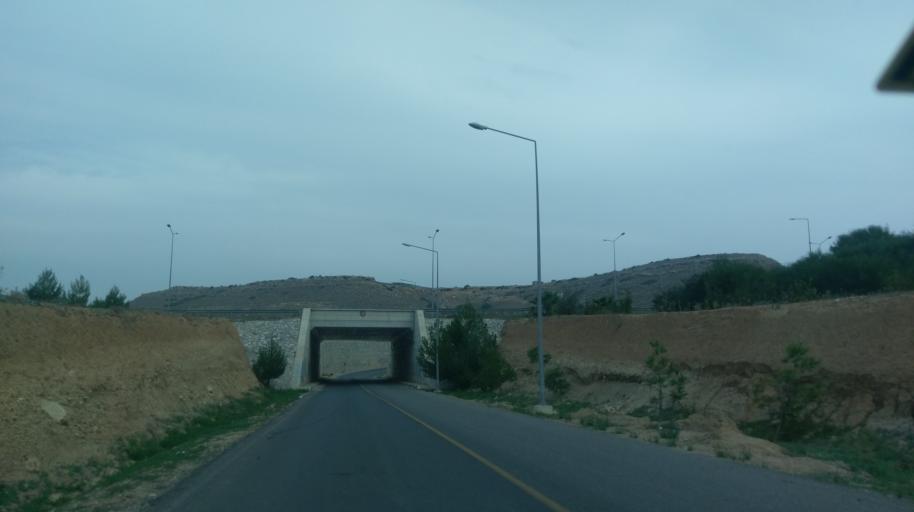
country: CY
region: Lefkosia
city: Akaki
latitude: 35.1943
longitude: 33.1082
